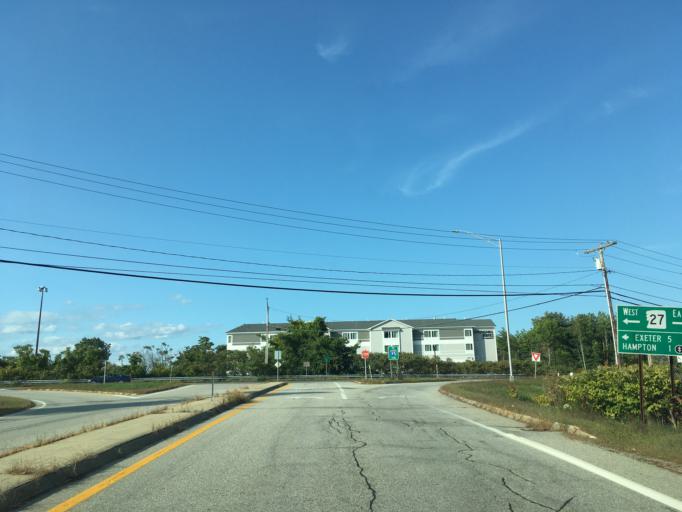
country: US
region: New Hampshire
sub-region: Rockingham County
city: Hampton
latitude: 42.9555
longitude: -70.8563
